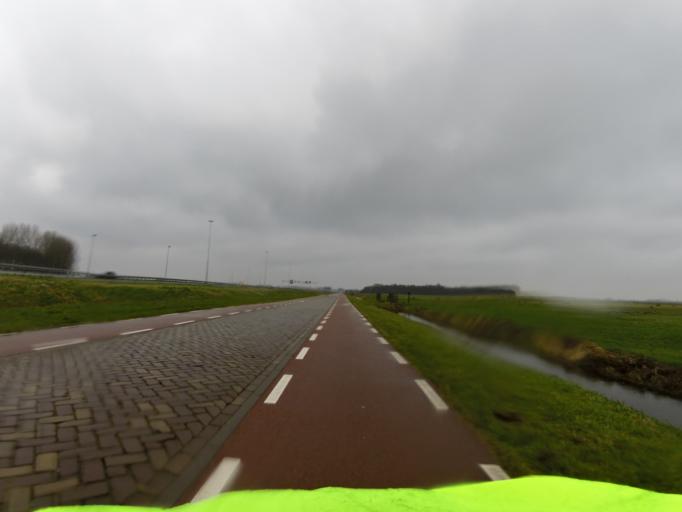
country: NL
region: South Holland
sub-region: Gemeente Vlaardingen
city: Vlaardingen
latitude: 51.9201
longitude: 4.3068
